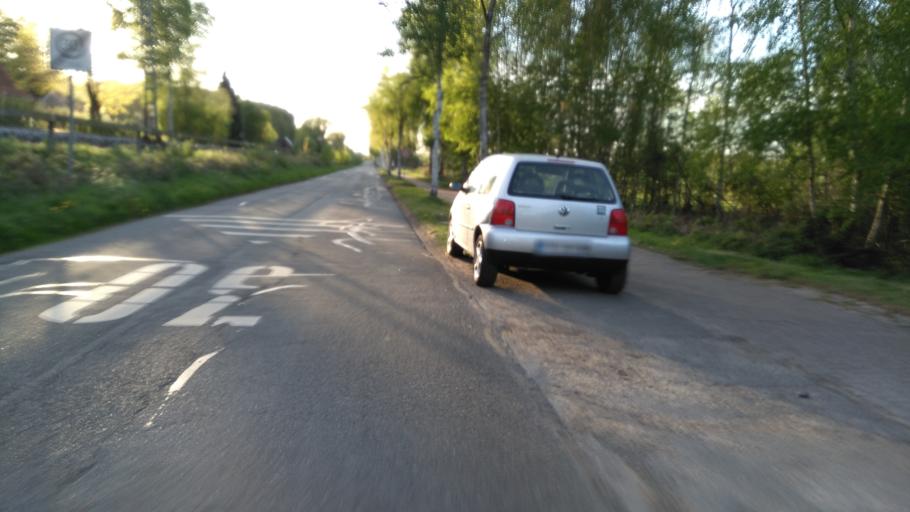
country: DE
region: Lower Saxony
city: Buxtehude
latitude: 53.4772
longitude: 9.6503
